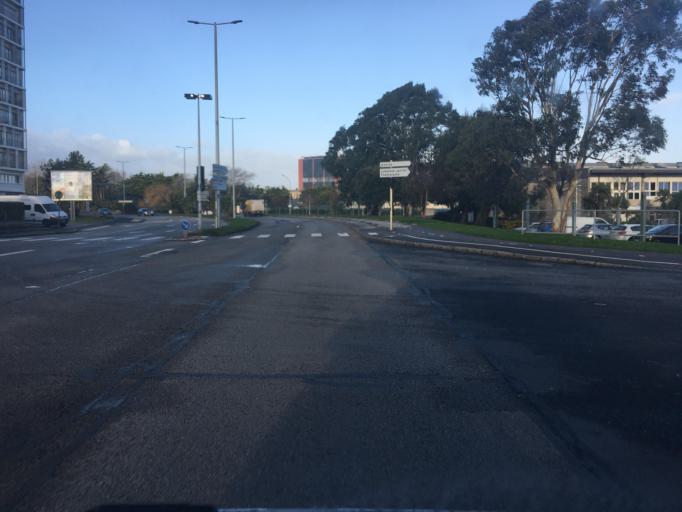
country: FR
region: Lower Normandy
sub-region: Departement de la Manche
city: Cherbourg-Octeville
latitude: 49.6445
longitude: -1.6268
